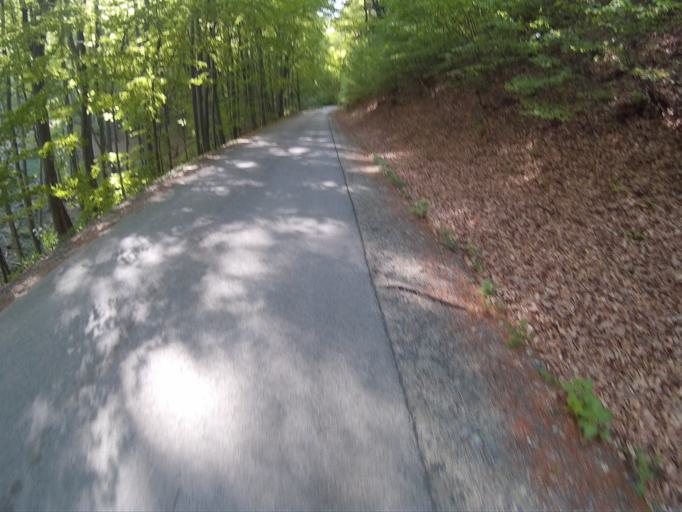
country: AT
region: Burgenland
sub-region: Politischer Bezirk Oberwart
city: Rechnitz
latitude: 47.3550
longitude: 16.4735
